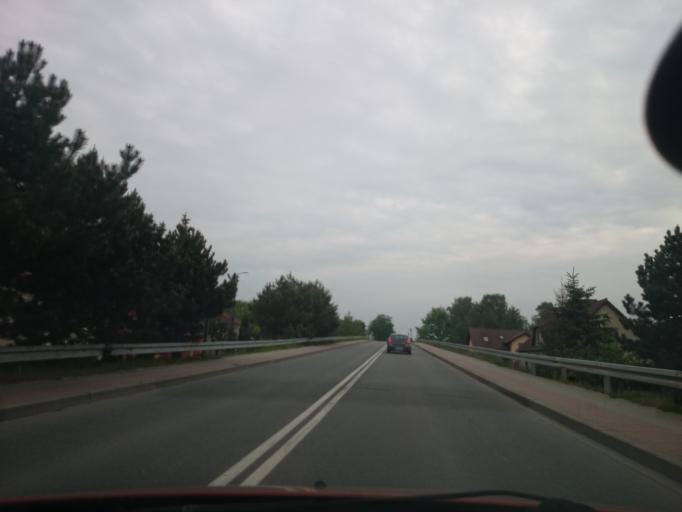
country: PL
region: Opole Voivodeship
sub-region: Powiat opolski
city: Dobrzen Wielki
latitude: 50.7740
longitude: 17.8559
